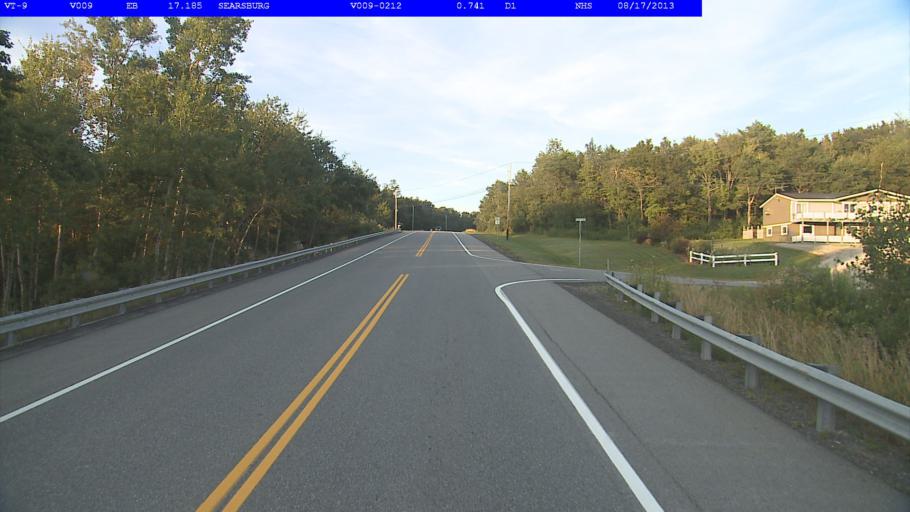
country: US
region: Vermont
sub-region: Windham County
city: Dover
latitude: 42.8933
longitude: -72.9970
